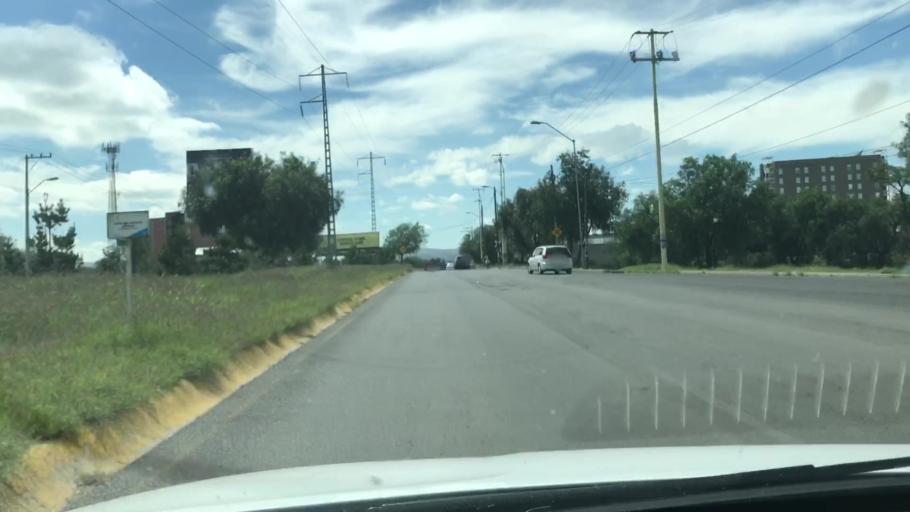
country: MX
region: Guanajuato
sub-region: Celaya
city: La Trinidad
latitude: 20.5361
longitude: -100.7778
